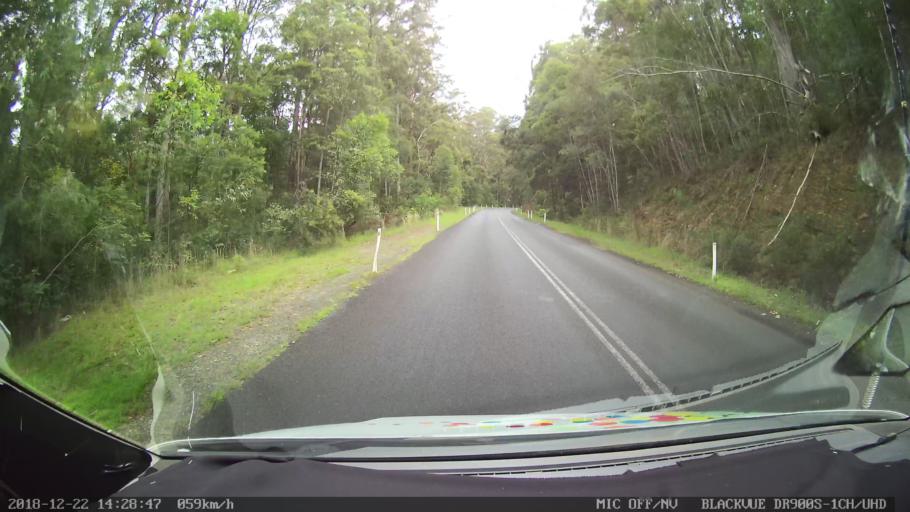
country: AU
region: New South Wales
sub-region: Bellingen
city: Dorrigo
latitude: -30.0756
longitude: 152.6370
